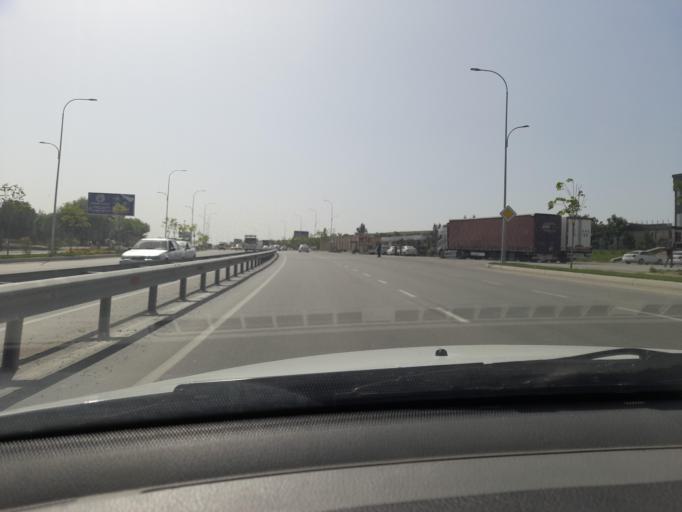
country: UZ
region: Samarqand
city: Jomboy
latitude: 39.6756
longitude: 67.0417
